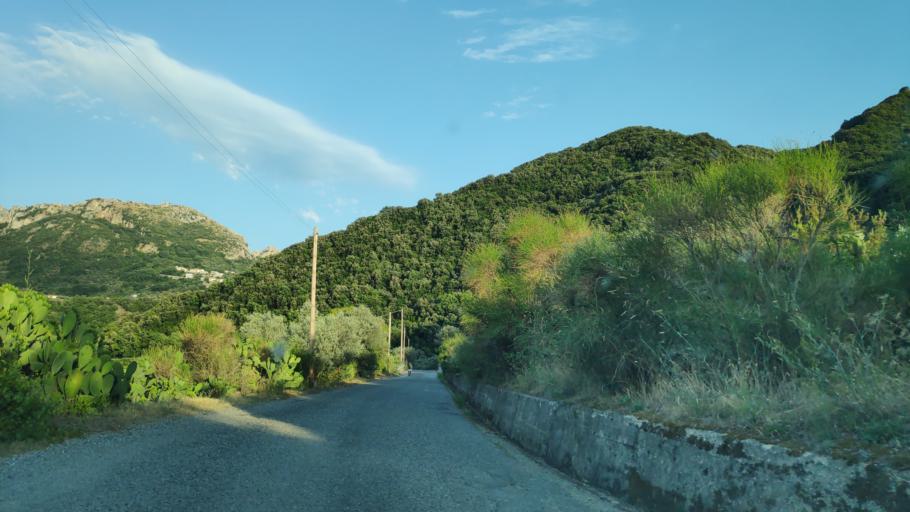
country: IT
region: Calabria
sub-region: Provincia di Reggio Calabria
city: Bivongi
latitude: 38.4851
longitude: 16.4356
